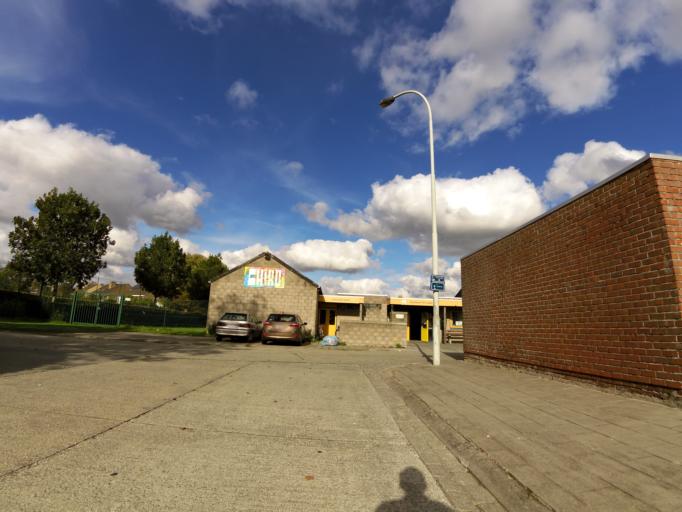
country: BE
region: Flanders
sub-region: Provincie West-Vlaanderen
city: Sint-Kruis
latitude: 51.2297
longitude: 3.2354
